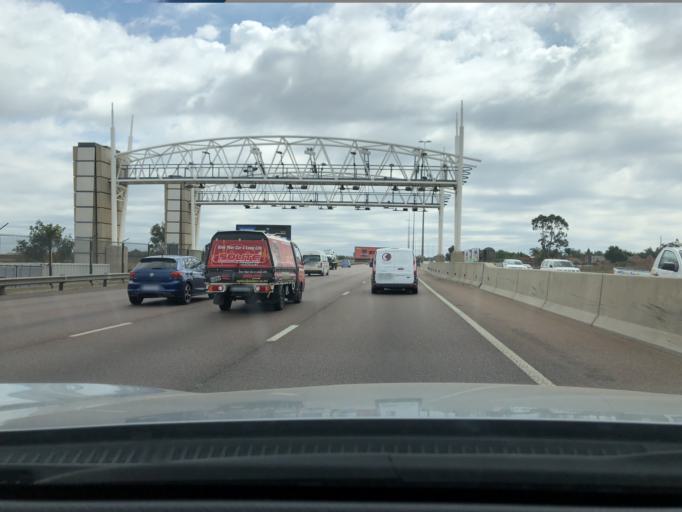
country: ZA
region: Gauteng
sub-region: City of Tshwane Metropolitan Municipality
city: Centurion
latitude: -25.8487
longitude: 28.2286
